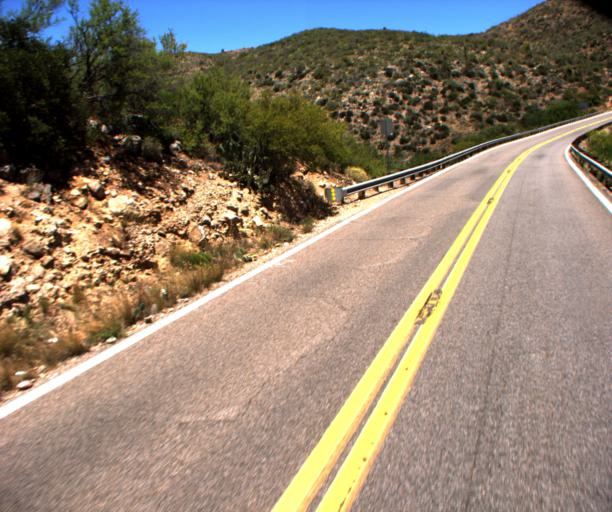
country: US
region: Arizona
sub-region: Pinal County
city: Kearny
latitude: 33.1875
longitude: -110.8091
